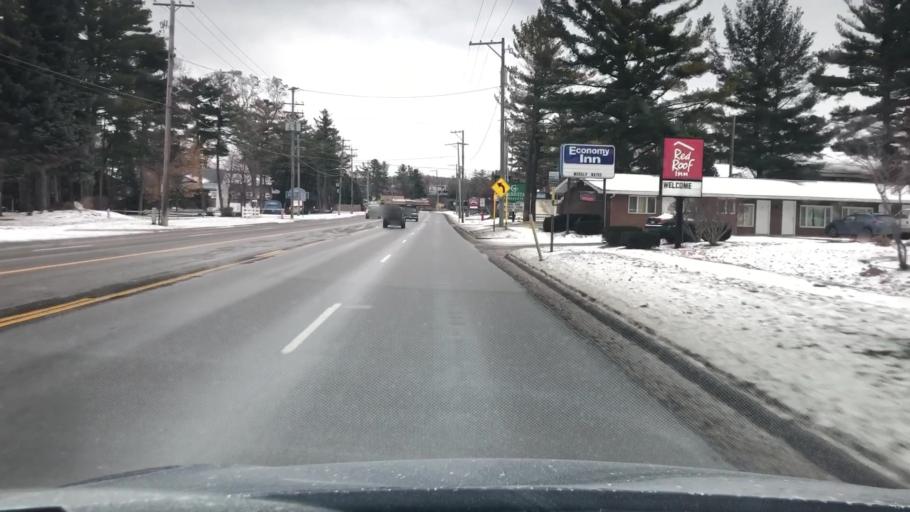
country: US
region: Michigan
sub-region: Grand Traverse County
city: Traverse City
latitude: 44.7462
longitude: -85.5449
